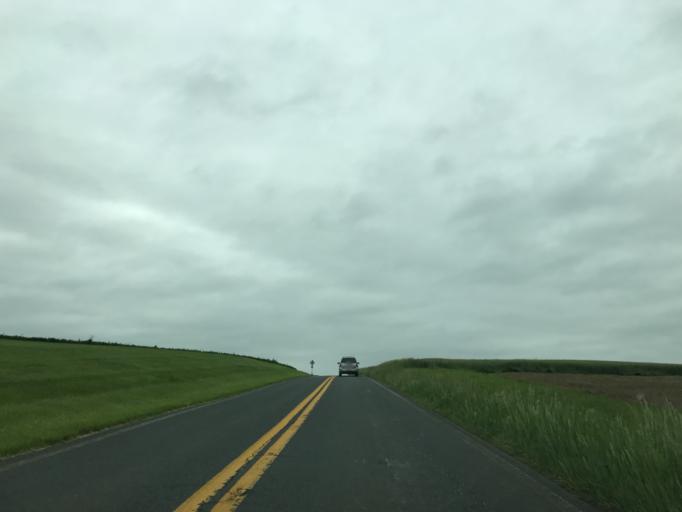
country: US
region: Maryland
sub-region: Carroll County
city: Hampstead
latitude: 39.5968
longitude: -76.9014
